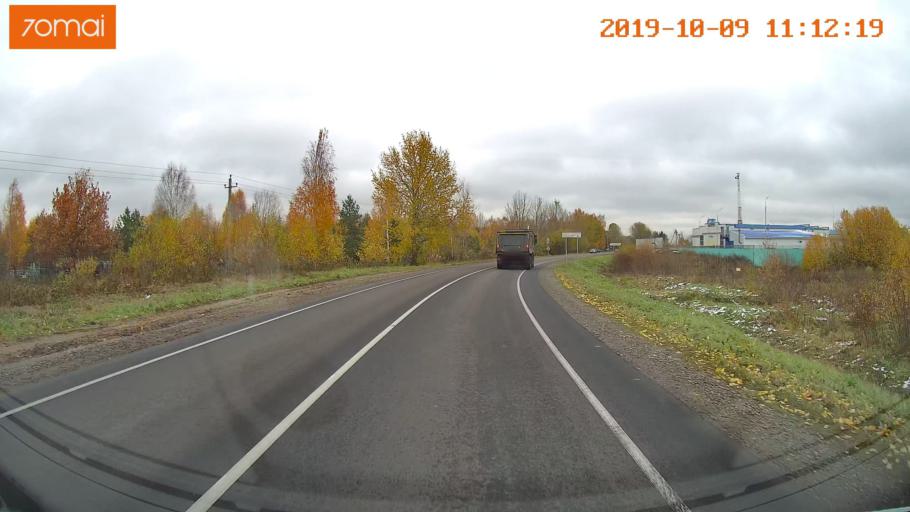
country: RU
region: Vologda
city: Vologda
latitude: 59.1766
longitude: 39.8290
